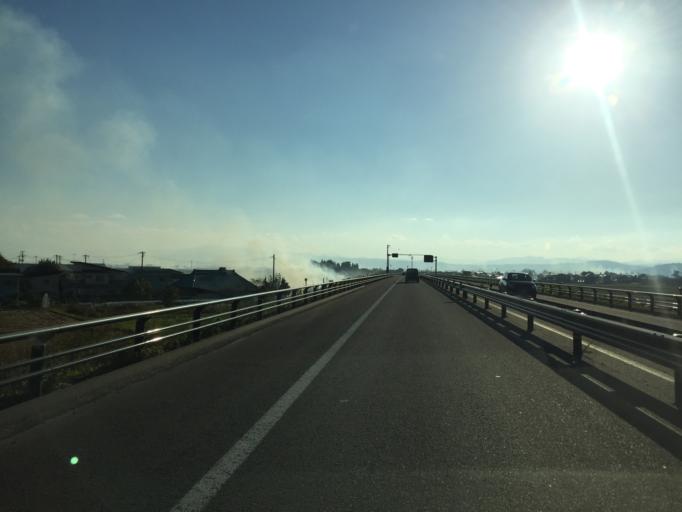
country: JP
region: Fukushima
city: Kitakata
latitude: 37.6347
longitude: 139.8864
